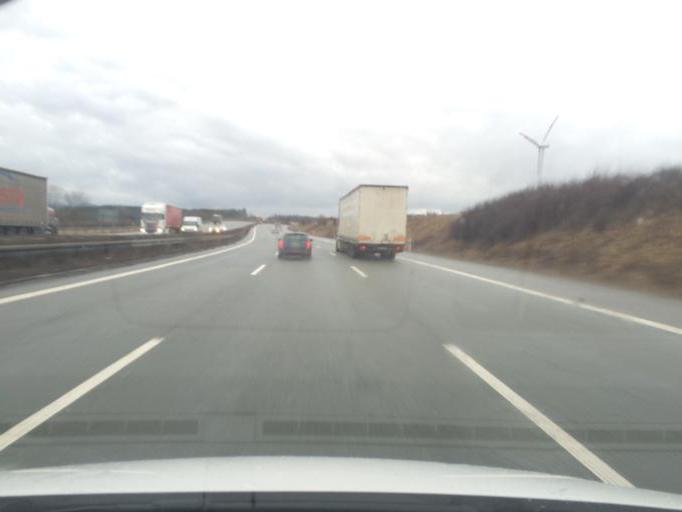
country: DE
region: Bavaria
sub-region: Upper Franconia
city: Berg
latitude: 50.3902
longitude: 11.7731
